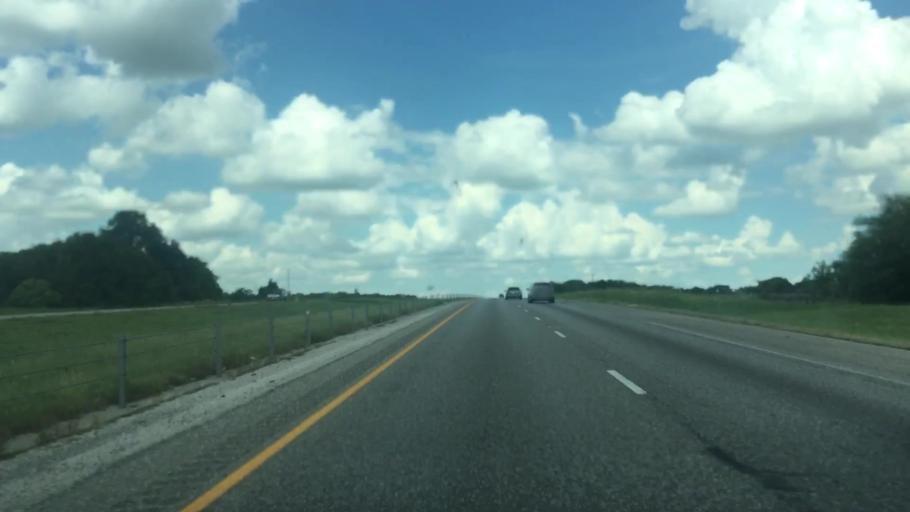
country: US
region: Texas
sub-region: Ellis County
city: Plum Grove
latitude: 32.0975
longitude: -97.0208
